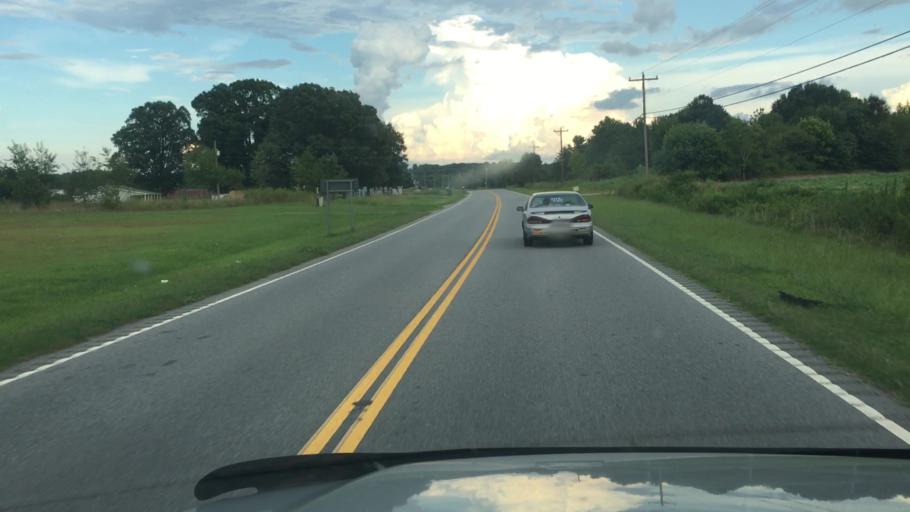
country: US
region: South Carolina
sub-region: Spartanburg County
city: Mayo
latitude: 35.1308
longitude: -81.7958
